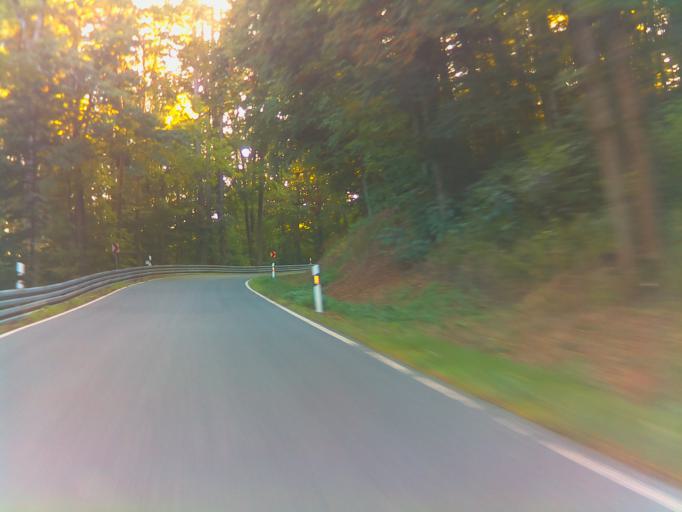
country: DE
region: Bavaria
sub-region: Regierungsbezirk Unterfranken
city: Hausen
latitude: 50.5095
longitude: 10.1048
